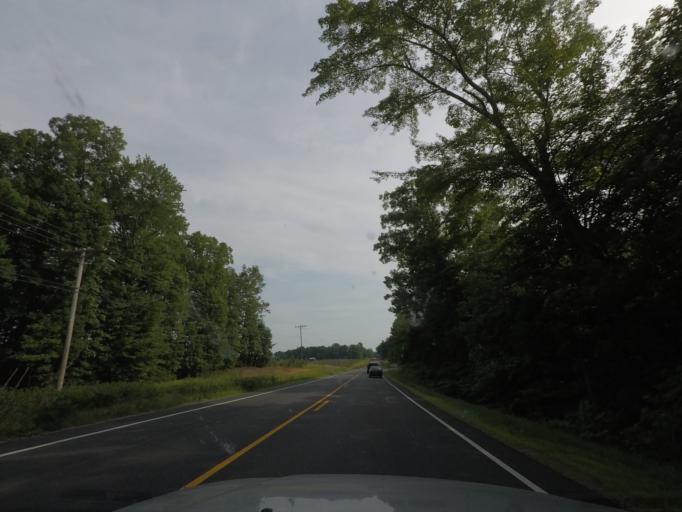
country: US
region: Virginia
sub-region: Prince Edward County
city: Hampden Sydney
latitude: 37.1404
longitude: -78.4446
